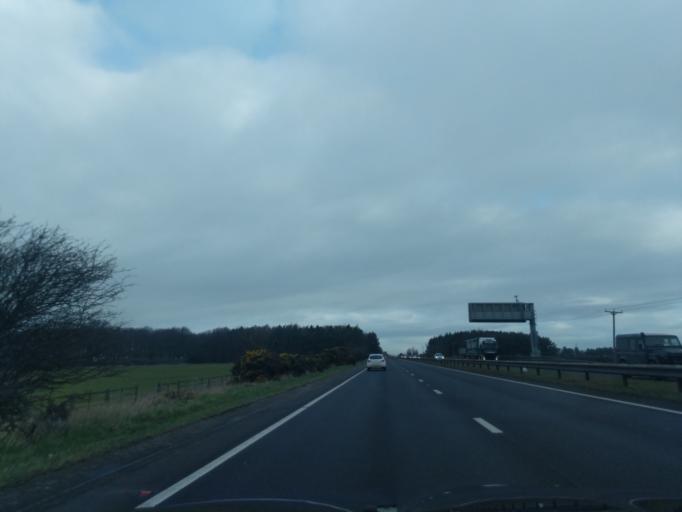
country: GB
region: England
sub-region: Newcastle upon Tyne
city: Hazlerigg
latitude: 55.0772
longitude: -1.6441
